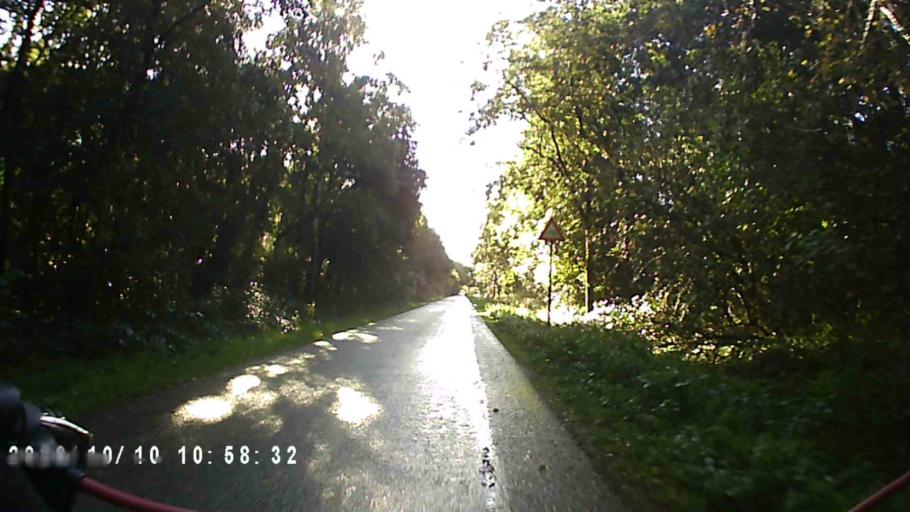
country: NL
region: Friesland
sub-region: Gemeente Achtkarspelen
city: Surhuisterveen
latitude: 53.1447
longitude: 6.2070
